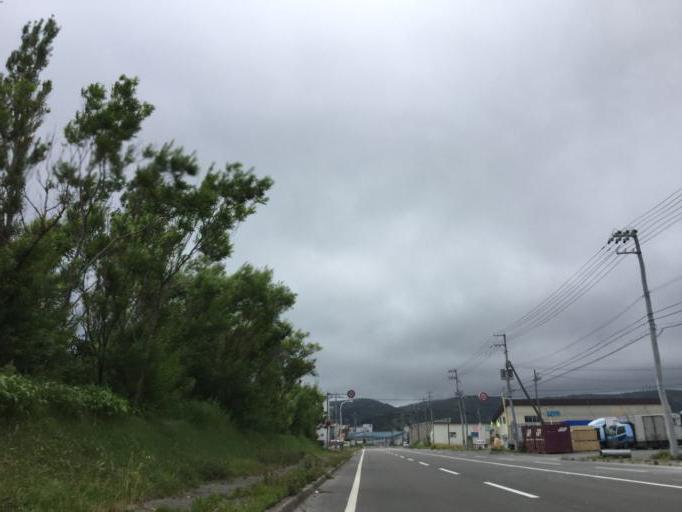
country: JP
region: Hokkaido
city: Wakkanai
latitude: 45.4003
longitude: 141.6957
